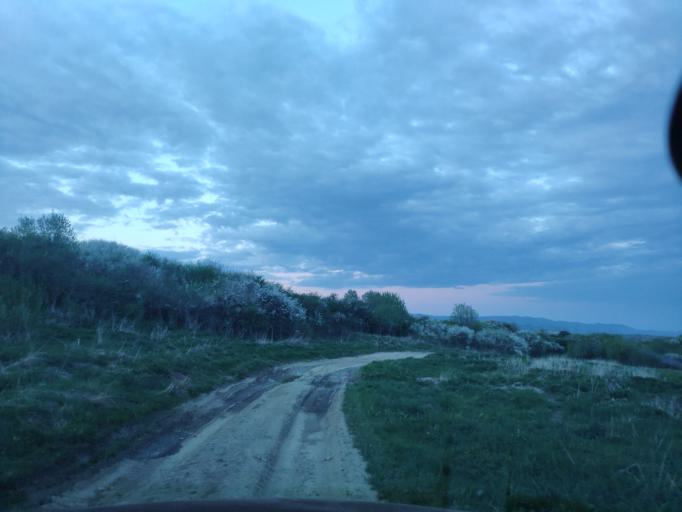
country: SK
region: Presovsky
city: Lipany
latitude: 49.1809
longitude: 20.8249
